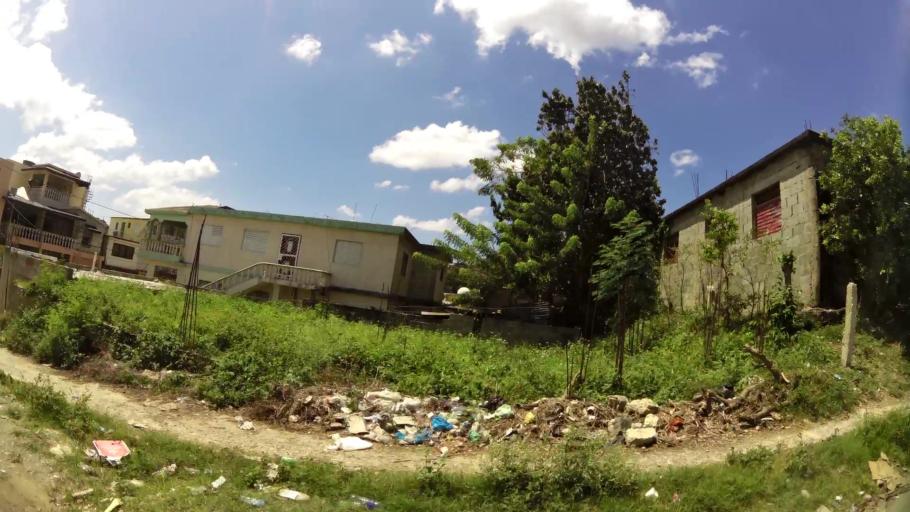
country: DO
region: San Cristobal
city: San Cristobal
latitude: 18.4038
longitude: -70.1092
